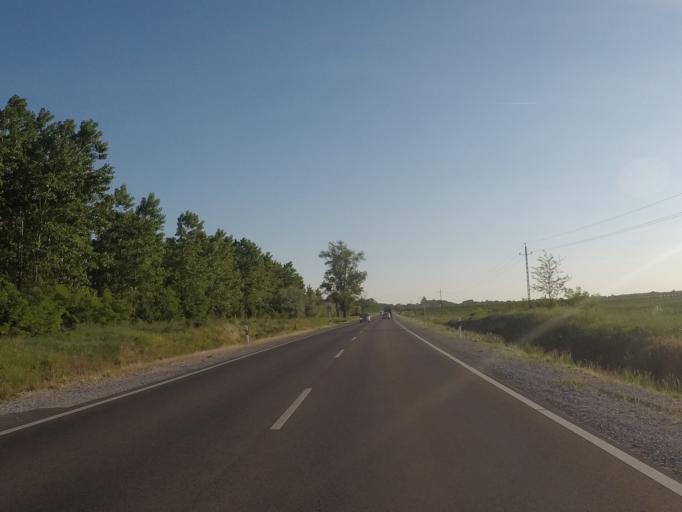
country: HU
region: Heves
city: Erdotelek
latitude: 47.6667
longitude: 20.3588
